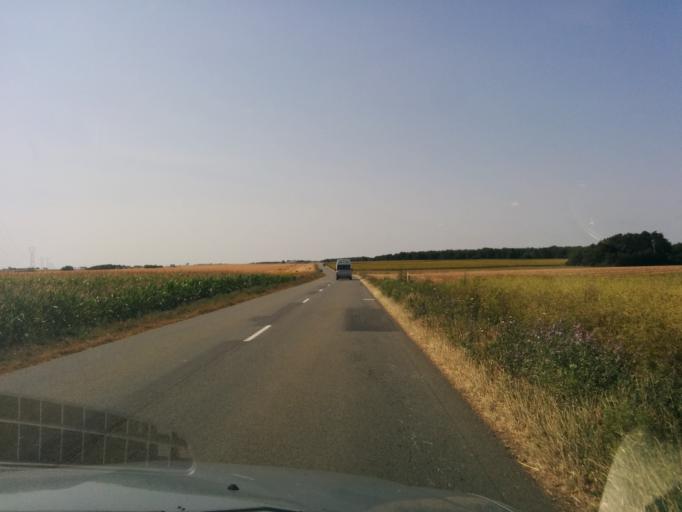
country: FR
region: Poitou-Charentes
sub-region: Departement de la Vienne
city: Neuville-de-Poitou
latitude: 46.7243
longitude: 0.2019
